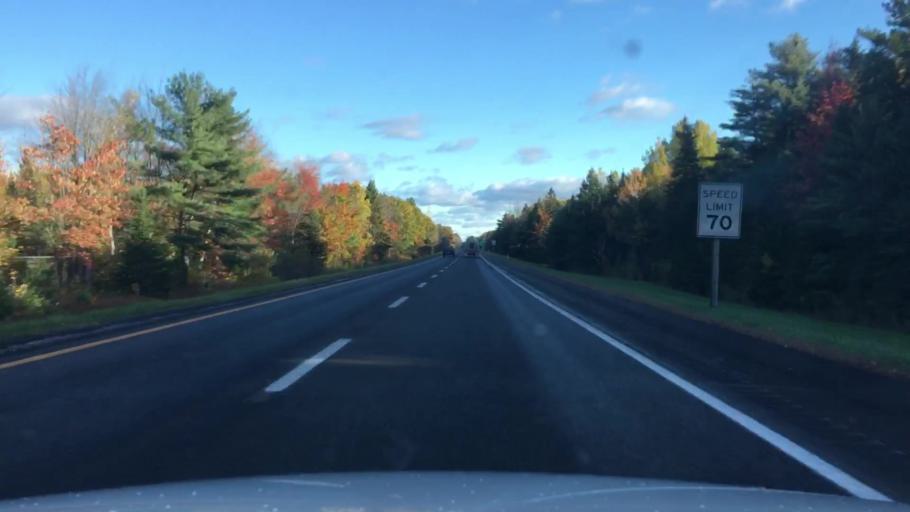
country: US
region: Maine
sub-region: Penobscot County
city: Orono
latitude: 44.8812
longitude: -68.6968
